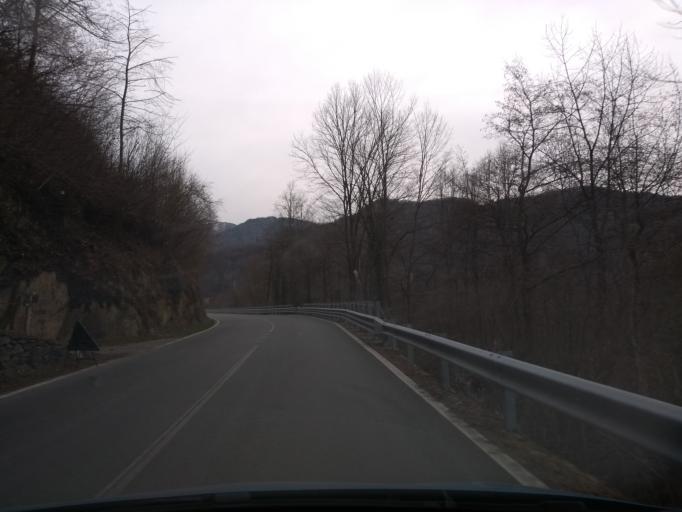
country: IT
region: Piedmont
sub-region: Provincia di Torino
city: Viu
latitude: 45.2387
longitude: 7.3882
